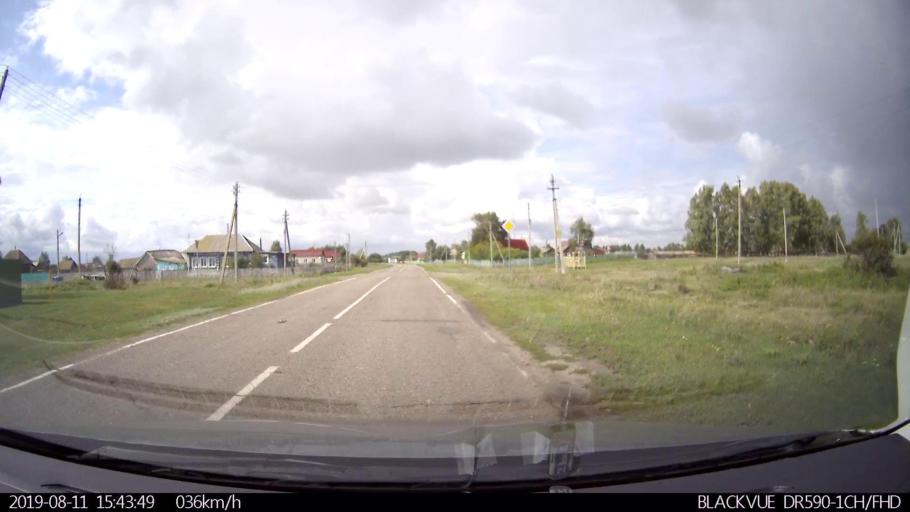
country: RU
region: Ulyanovsk
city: Ignatovka
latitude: 53.8783
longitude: 47.6585
